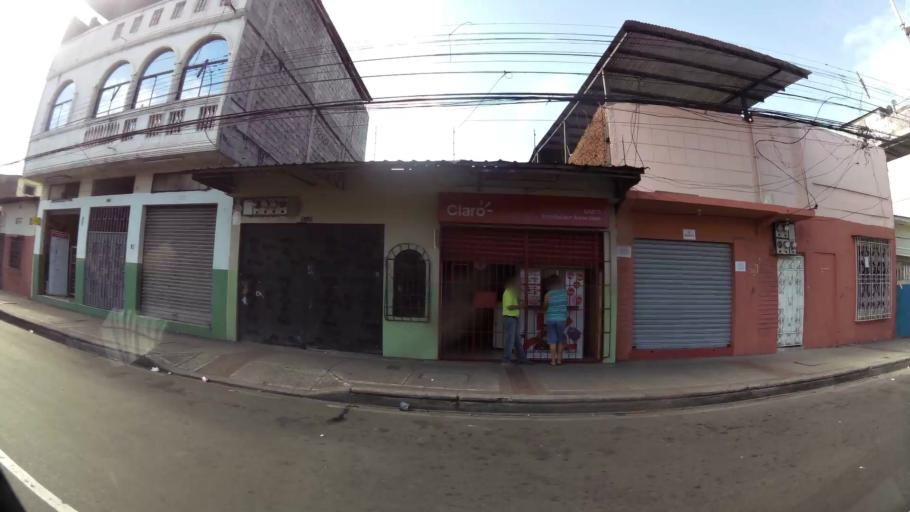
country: EC
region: Guayas
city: Guayaquil
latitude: -2.1995
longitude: -79.9244
